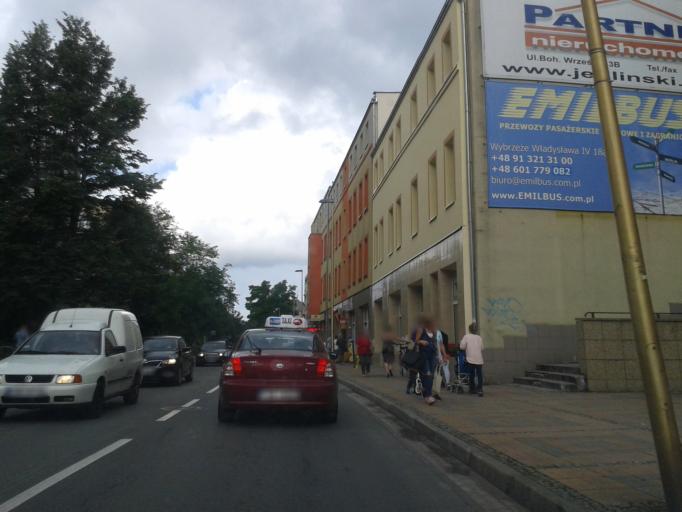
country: PL
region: West Pomeranian Voivodeship
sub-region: Swinoujscie
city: Swinoujscie
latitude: 53.9102
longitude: 14.2441
